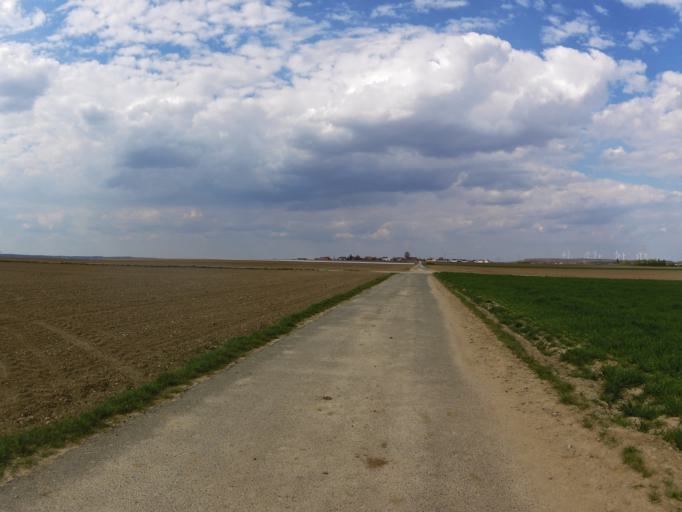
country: DE
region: Bavaria
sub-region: Regierungsbezirk Unterfranken
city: Oberpleichfeld
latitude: 49.8641
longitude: 10.0938
